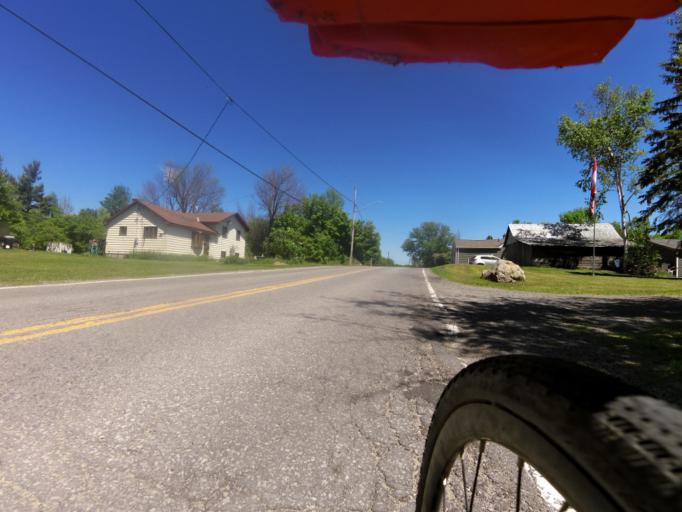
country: CA
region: Ontario
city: Carleton Place
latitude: 45.1907
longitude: -76.3306
